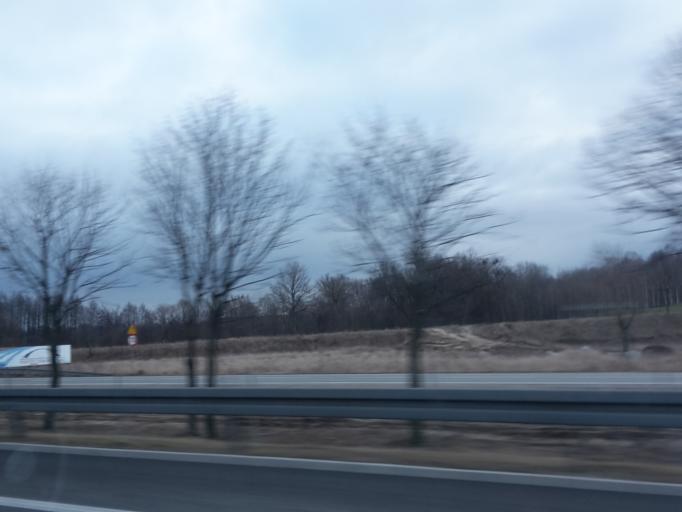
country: PL
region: Warmian-Masurian Voivodeship
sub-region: Powiat elblaski
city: Paslek
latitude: 54.0219
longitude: 19.6755
